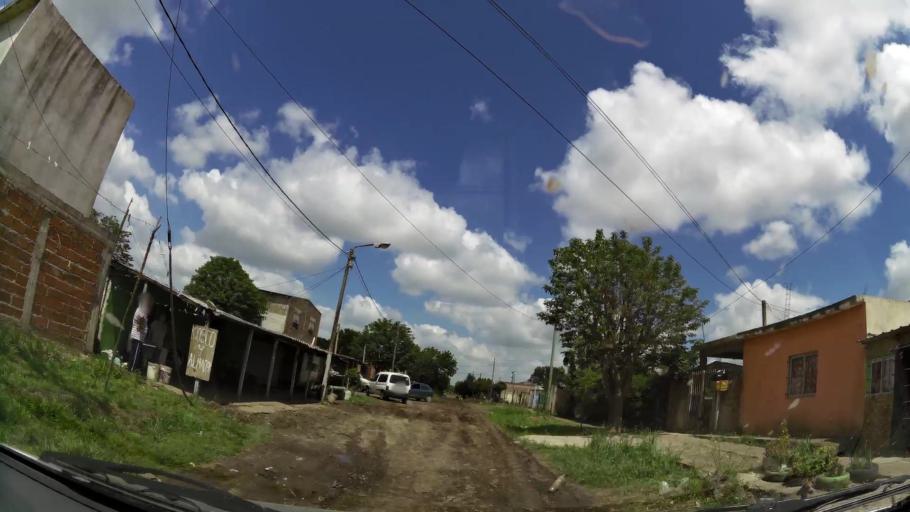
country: AR
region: Buenos Aires
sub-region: Partido de Quilmes
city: Quilmes
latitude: -34.8402
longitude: -58.2292
